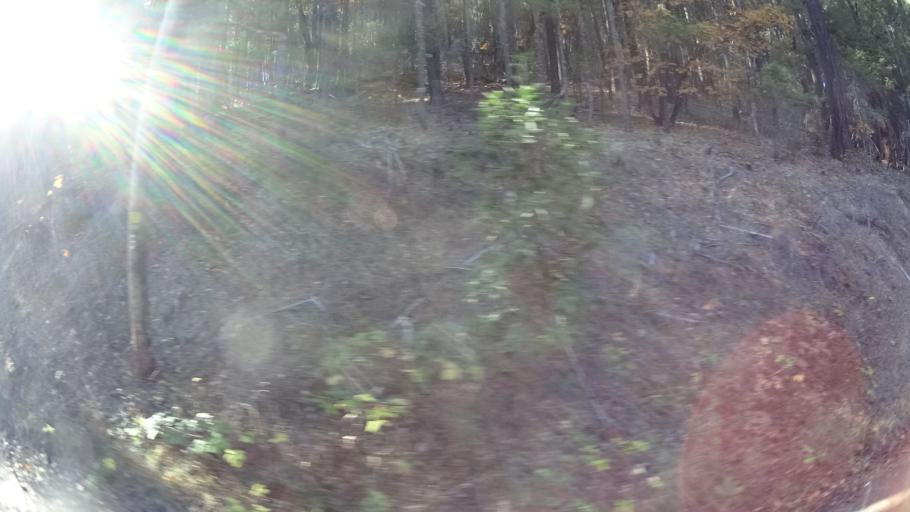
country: US
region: California
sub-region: Siskiyou County
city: Yreka
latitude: 41.8258
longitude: -122.9775
